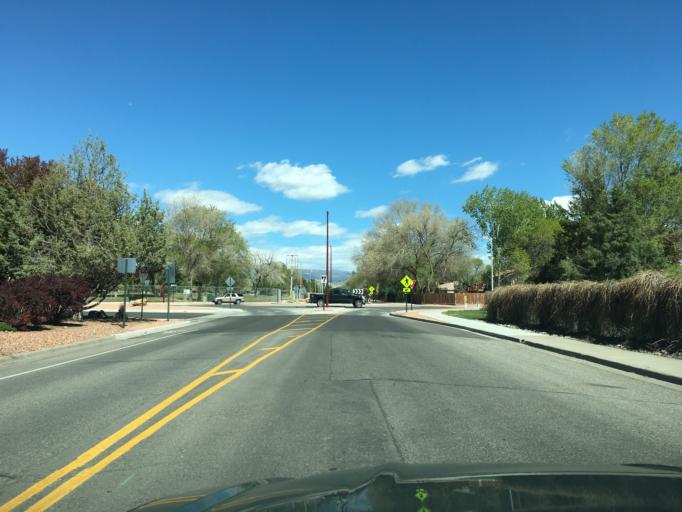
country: US
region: Colorado
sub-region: Montrose County
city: Montrose
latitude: 38.4745
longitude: -107.8575
